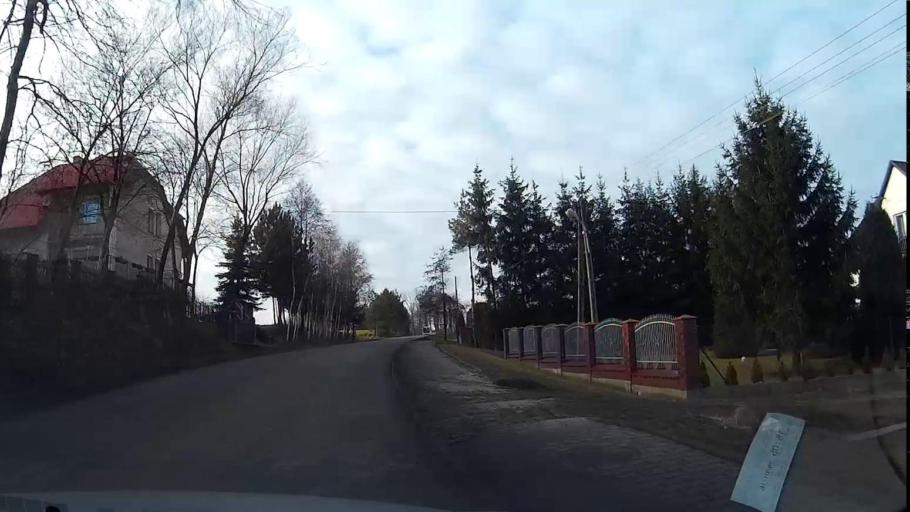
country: PL
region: Lesser Poland Voivodeship
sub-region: Powiat krakowski
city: Czulow
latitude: 50.0626
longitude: 19.6875
